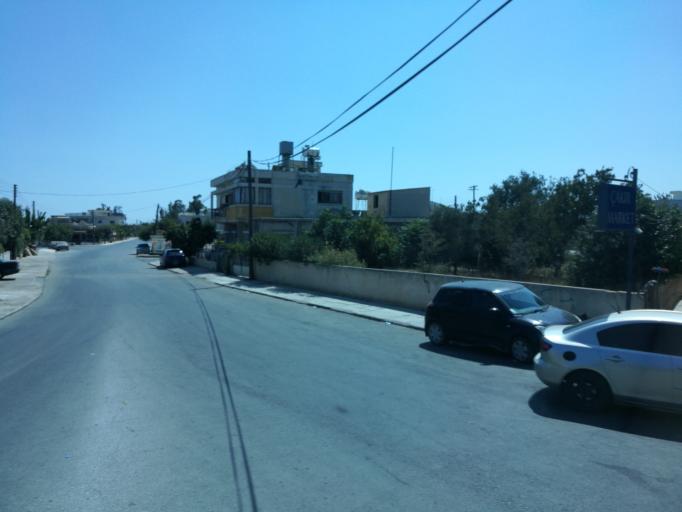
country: CY
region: Ammochostos
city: Famagusta
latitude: 35.1062
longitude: 33.9486
